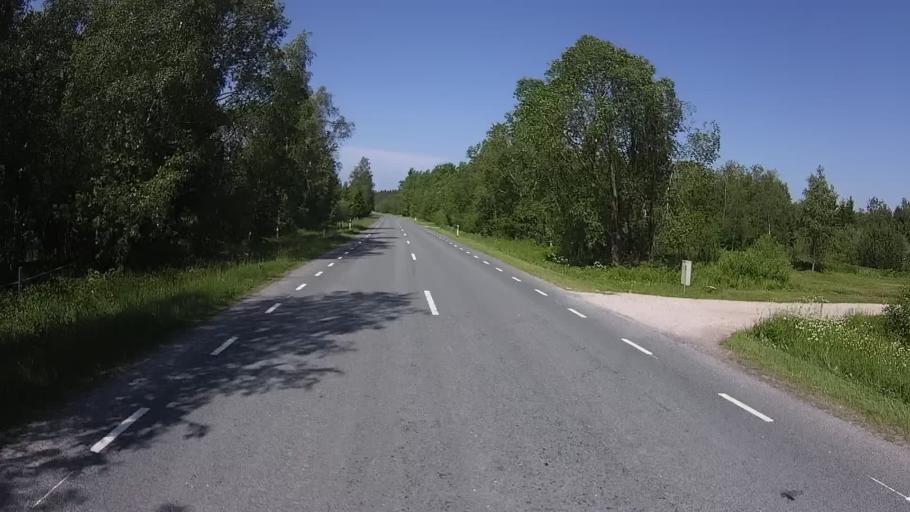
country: EE
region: Saare
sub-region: Kuressaare linn
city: Kuressaare
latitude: 58.3918
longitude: 22.4323
